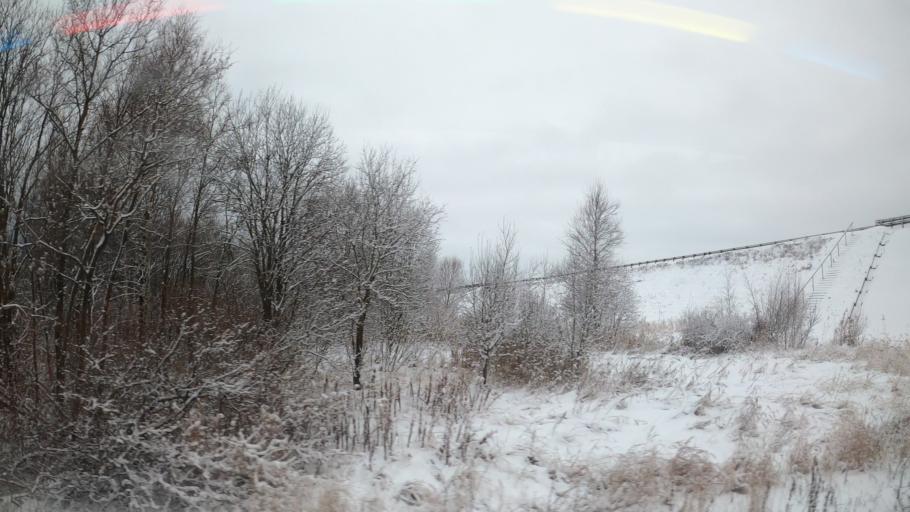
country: RU
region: Jaroslavl
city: Pereslavl'-Zalesskiy
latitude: 56.7153
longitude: 38.9098
